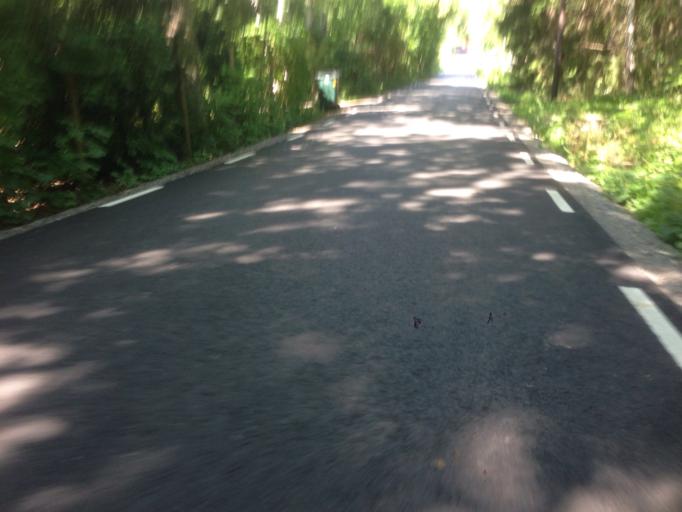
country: SE
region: Stockholm
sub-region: Vaxholms Kommun
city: Vaxholm
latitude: 59.3810
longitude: 18.3744
